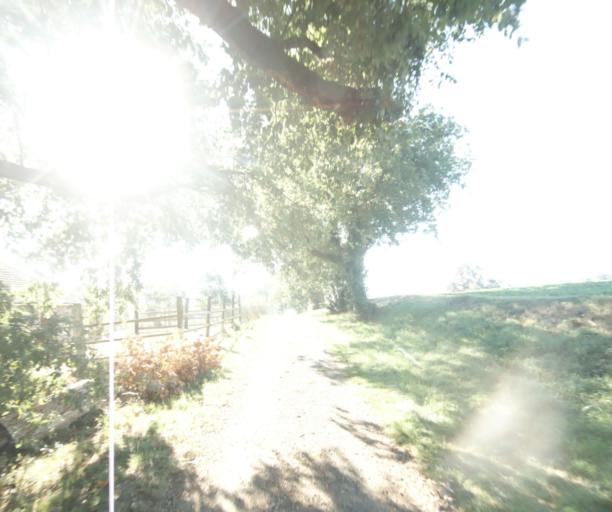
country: FR
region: Midi-Pyrenees
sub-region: Departement du Gers
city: Vic-Fezensac
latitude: 43.8173
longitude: 0.2702
